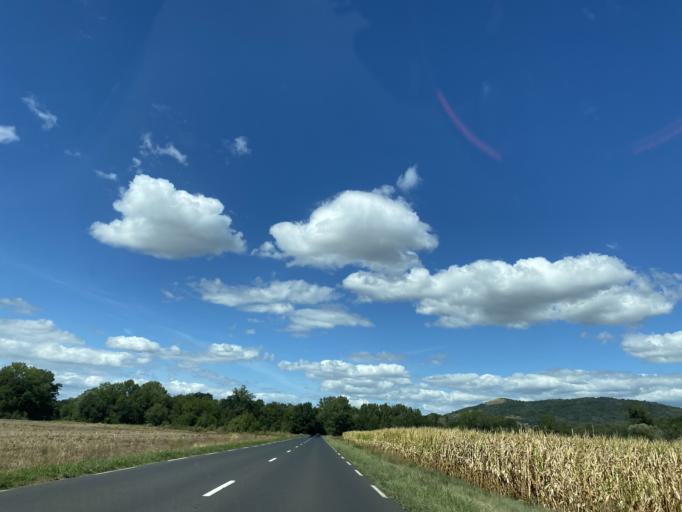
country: FR
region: Auvergne
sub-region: Departement du Puy-de-Dome
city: Perignat-sur-Allier
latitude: 45.7365
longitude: 3.2299
